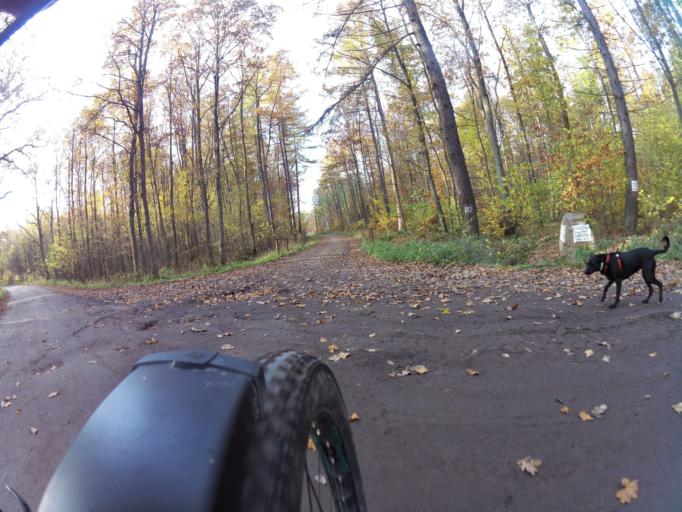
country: PL
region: Pomeranian Voivodeship
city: Strzelno
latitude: 54.7415
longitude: 18.2516
